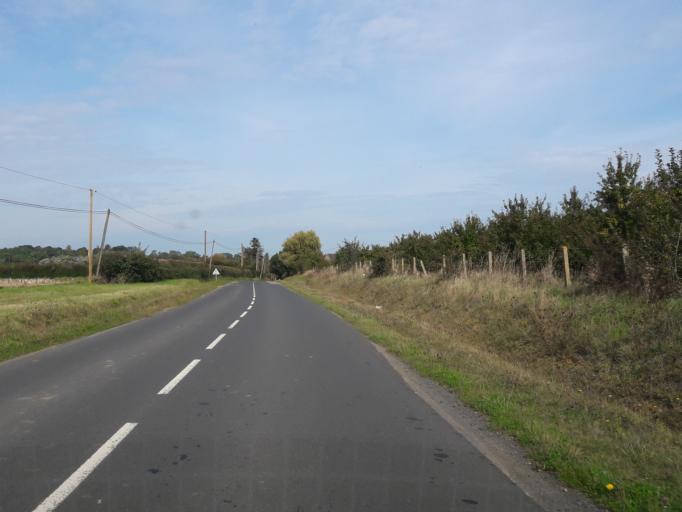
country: FR
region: Lower Normandy
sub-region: Departement du Calvados
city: Bayeux
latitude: 49.2399
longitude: -0.7037
